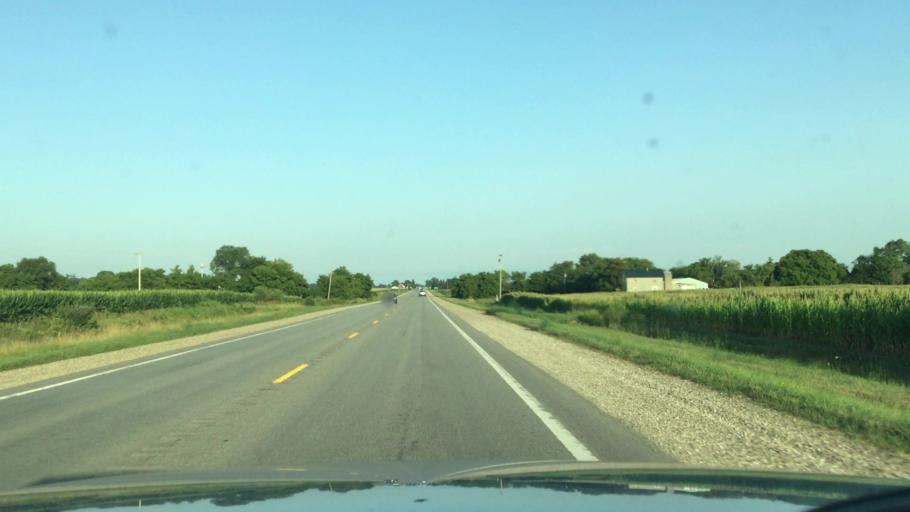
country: US
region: Michigan
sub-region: Gratiot County
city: Ithaca
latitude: 43.1760
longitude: -84.5735
